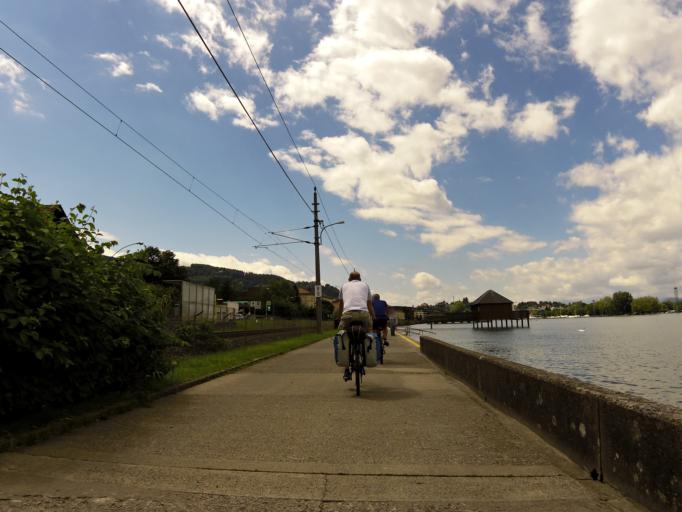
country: AT
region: Vorarlberg
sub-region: Politischer Bezirk Bregenz
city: Bregenz
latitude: 47.5123
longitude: 9.7530
